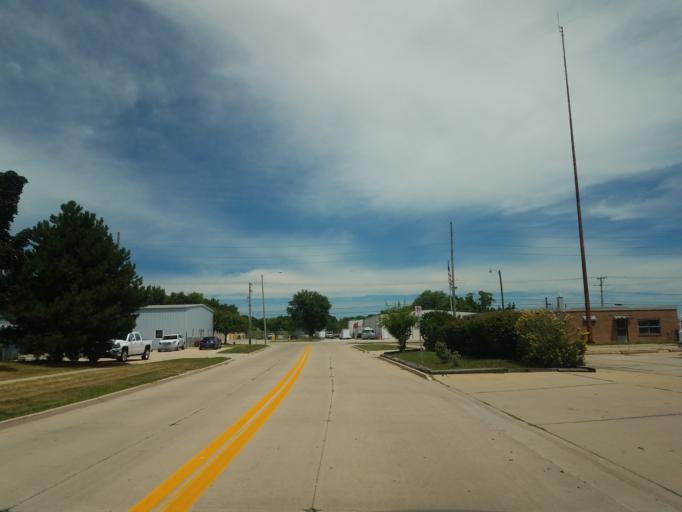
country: US
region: Illinois
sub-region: McLean County
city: Bloomington
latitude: 40.4625
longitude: -88.9883
